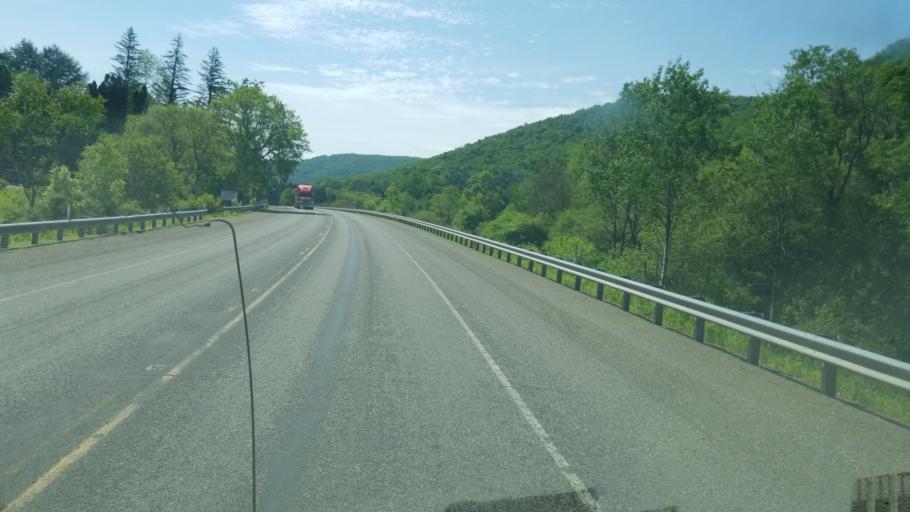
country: US
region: Pennsylvania
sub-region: Potter County
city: Galeton
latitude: 41.7610
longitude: -77.6880
